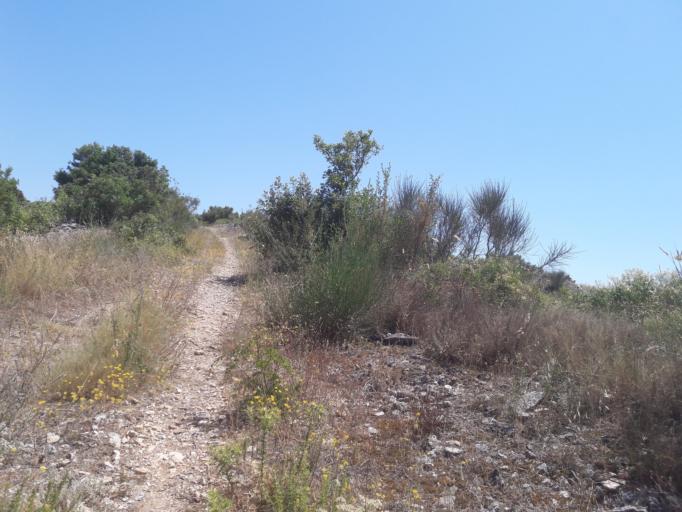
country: HR
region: Sibensko-Kniniska
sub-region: Grad Sibenik
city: Sibenik
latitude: 43.6931
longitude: 15.8539
